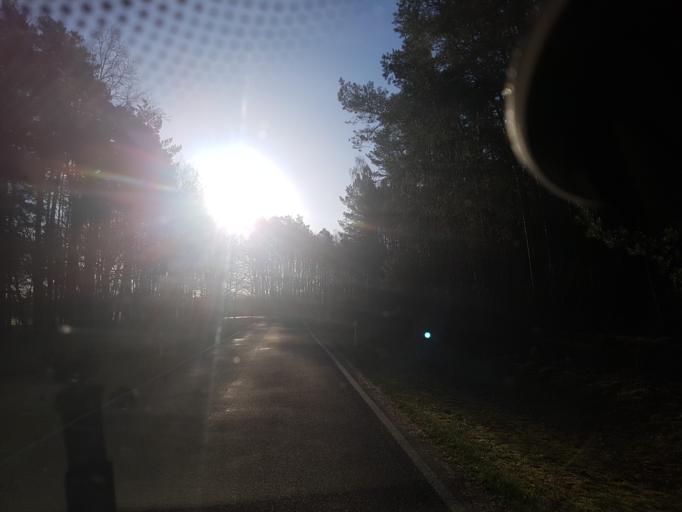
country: DE
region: Brandenburg
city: Lieberose
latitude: 52.0376
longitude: 14.3181
